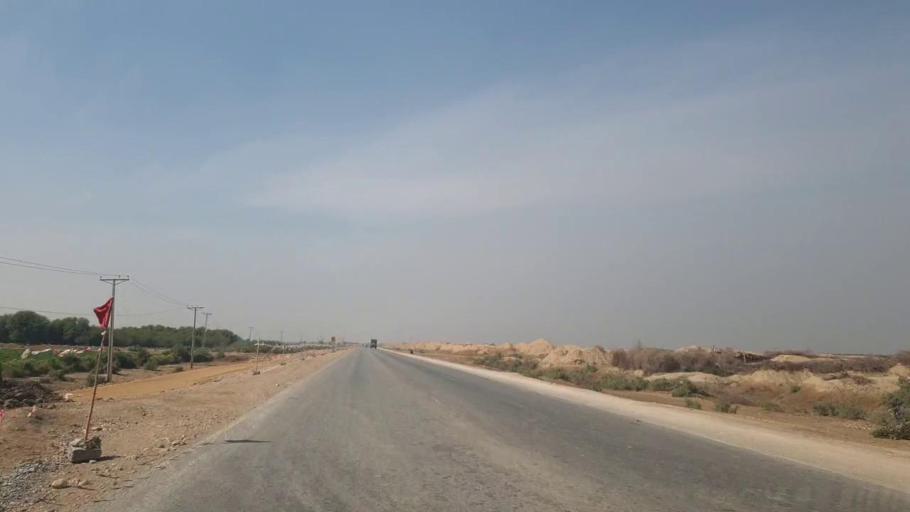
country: PK
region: Sindh
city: Sann
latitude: 26.0033
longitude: 68.1587
